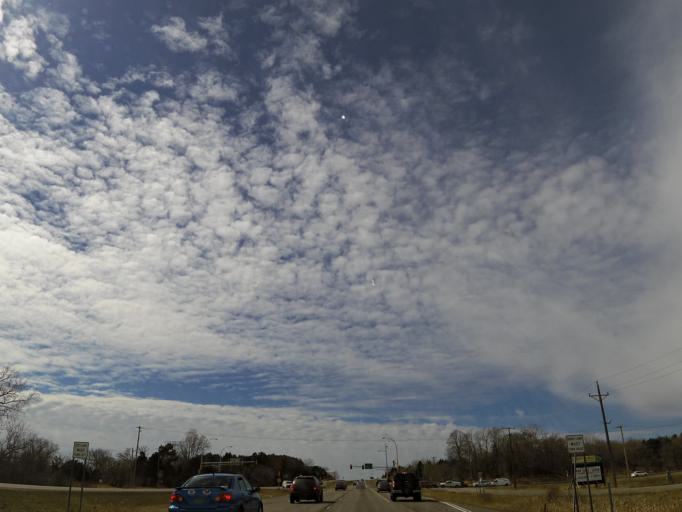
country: US
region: Minnesota
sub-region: Washington County
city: Lake Elmo
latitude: 45.0360
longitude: -92.8613
